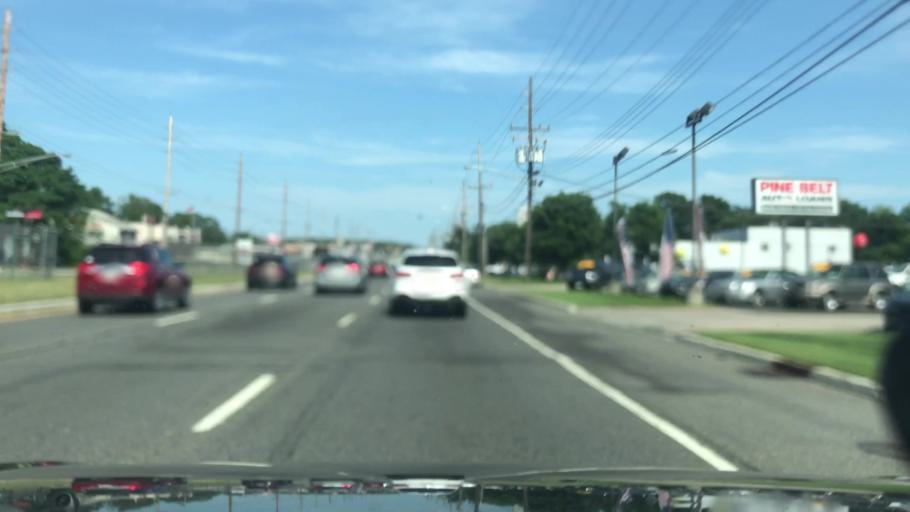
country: US
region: New Jersey
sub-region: Ocean County
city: Toms River
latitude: 39.9636
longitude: -74.1935
